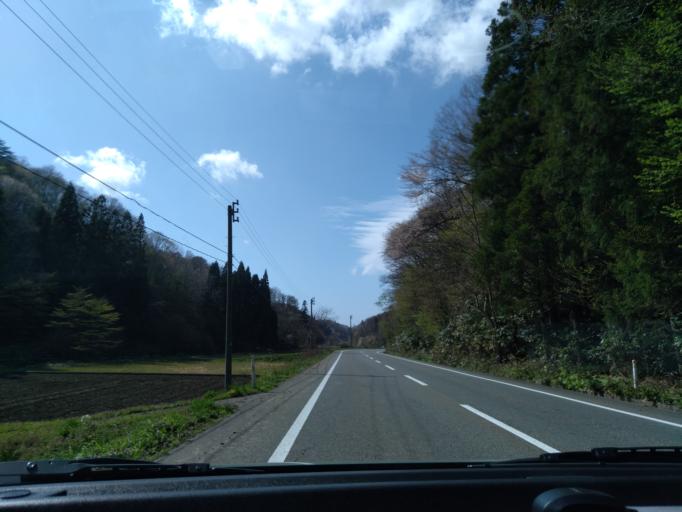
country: JP
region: Akita
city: Akita
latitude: 39.7031
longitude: 140.2156
